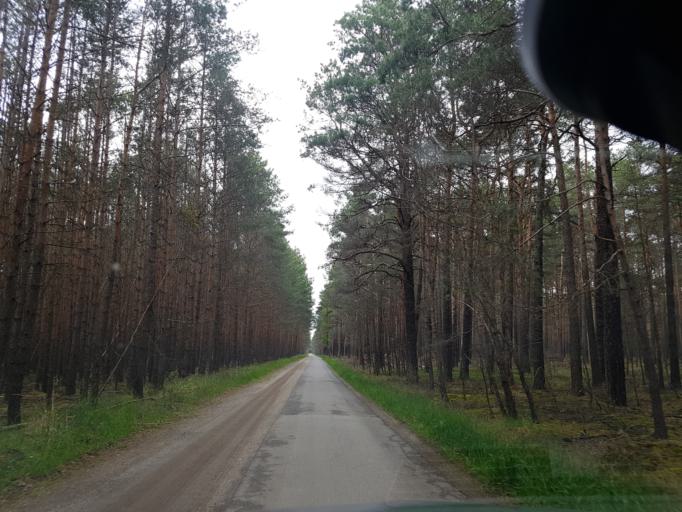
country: DE
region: Brandenburg
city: Crinitz
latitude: 51.6719
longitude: 13.7823
